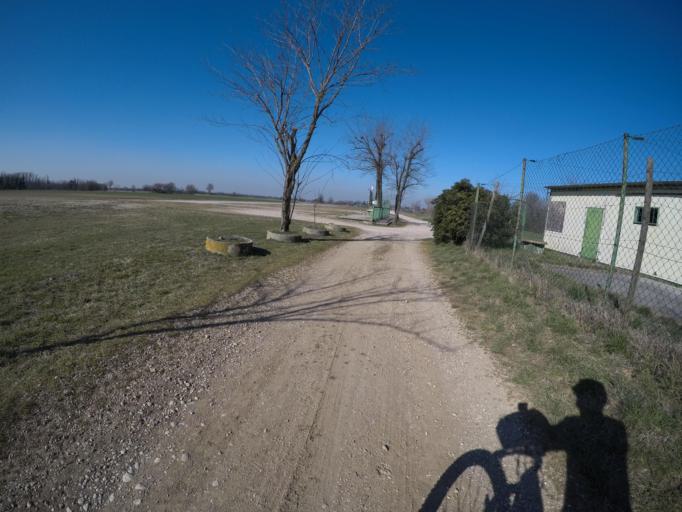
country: IT
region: Friuli Venezia Giulia
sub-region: Provincia di Udine
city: Pasian di Prato
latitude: 46.0182
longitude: 13.1865
